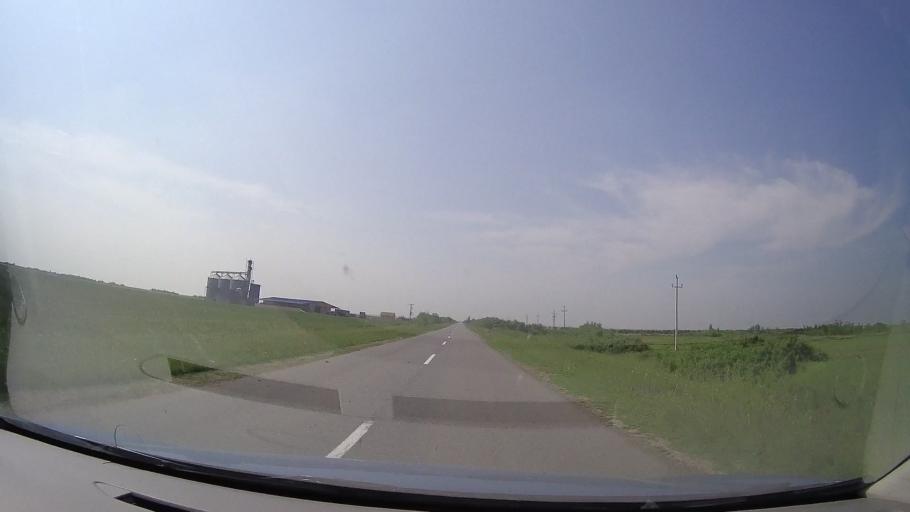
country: RS
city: Jarkovac
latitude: 45.2556
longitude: 20.7637
